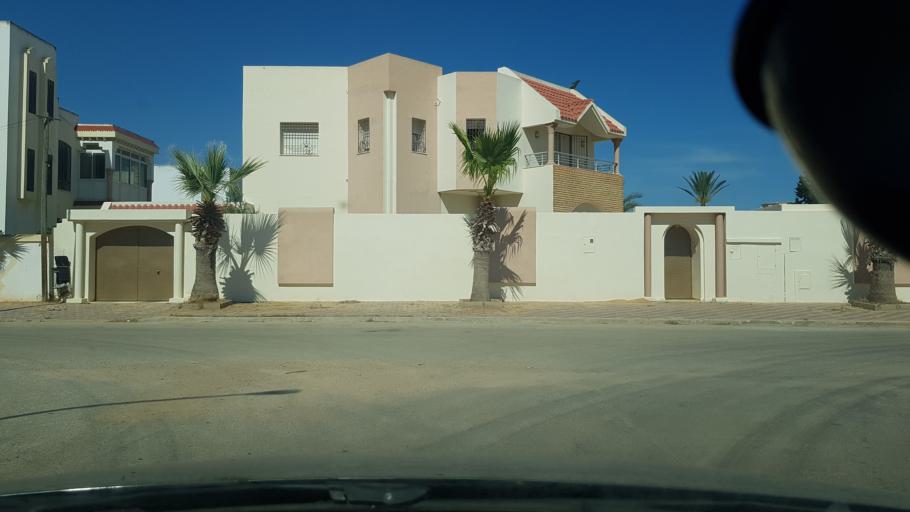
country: TN
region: Safaqis
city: Al Qarmadah
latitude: 34.8294
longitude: 10.7594
